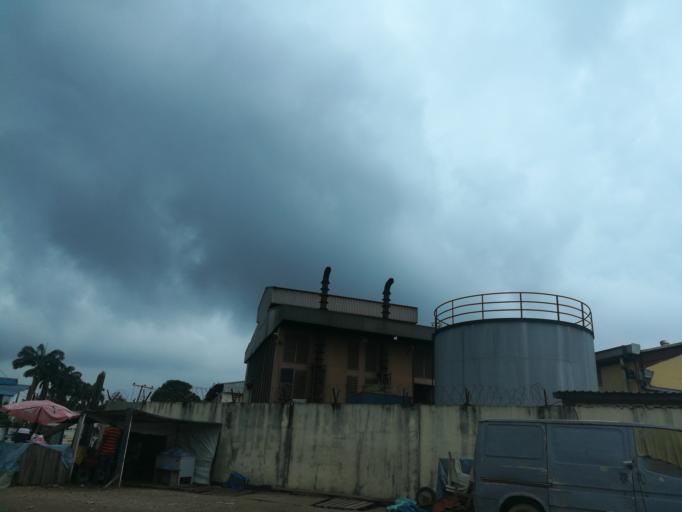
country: NG
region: Lagos
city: Agege
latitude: 6.6175
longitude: 3.3400
